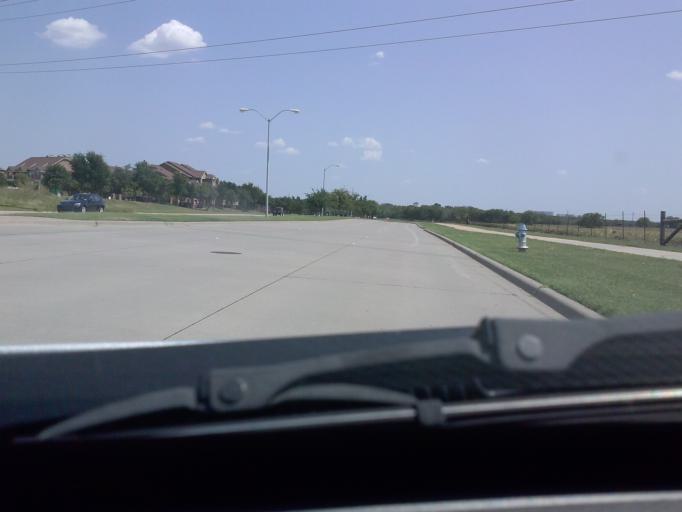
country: US
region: Texas
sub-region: Denton County
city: The Colony
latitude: 33.0614
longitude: -96.8114
